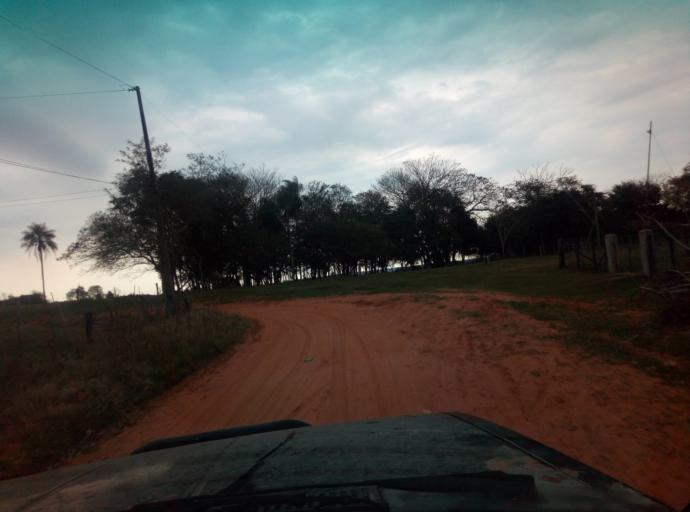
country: PY
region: Caaguazu
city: Doctor Cecilio Baez
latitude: -25.1389
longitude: -56.2232
